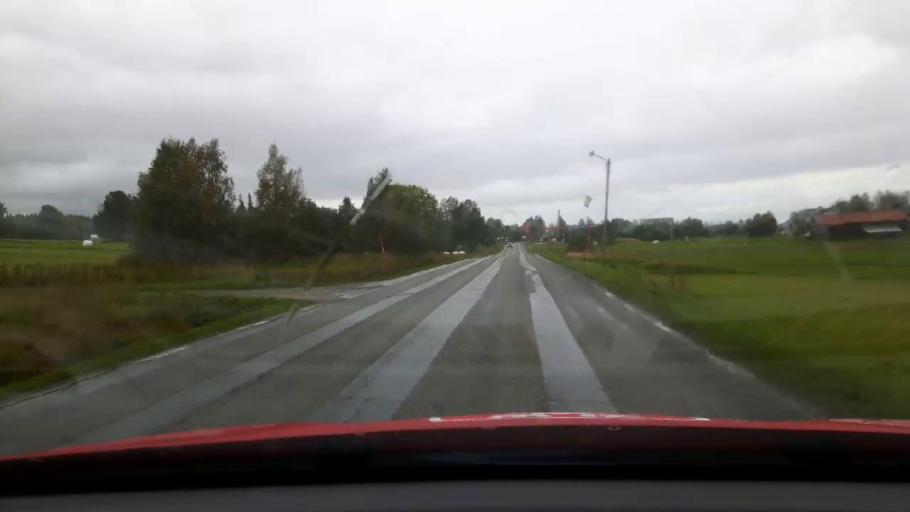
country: SE
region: Jaemtland
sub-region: Bergs Kommun
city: Hoverberg
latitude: 62.8360
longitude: 14.3847
